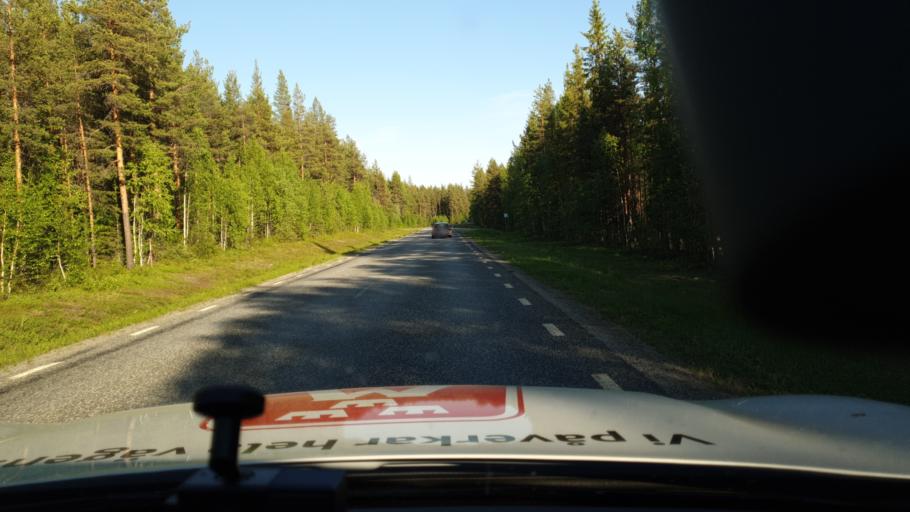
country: SE
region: Vaesterbotten
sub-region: Lycksele Kommun
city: Lycksele
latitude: 64.5949
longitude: 18.5481
